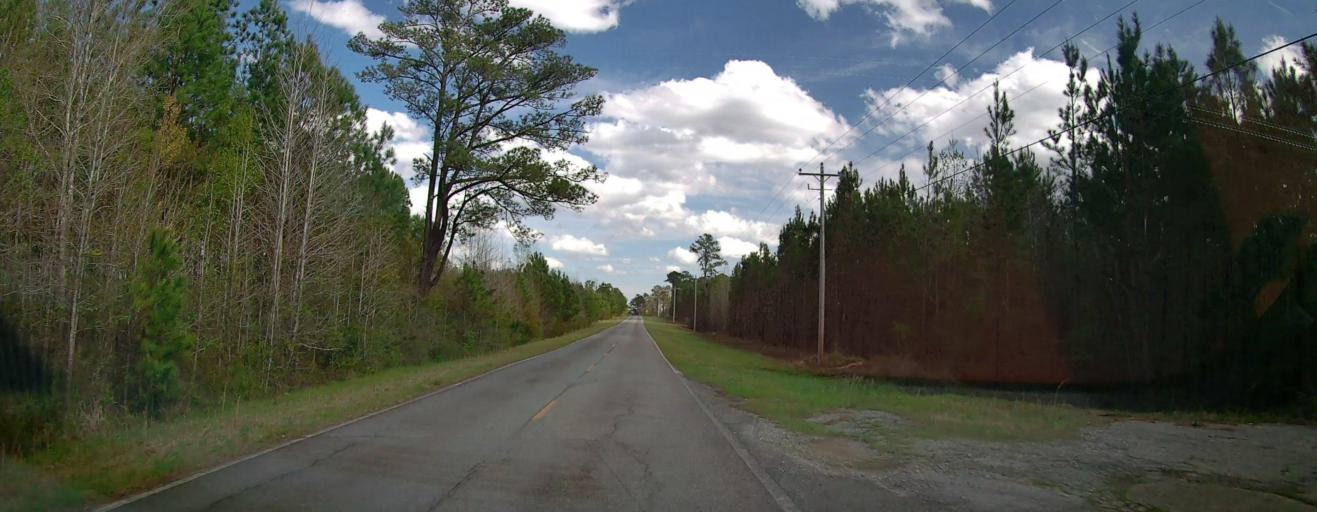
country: US
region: Georgia
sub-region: Wilkinson County
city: Gordon
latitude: 32.8028
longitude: -83.4294
